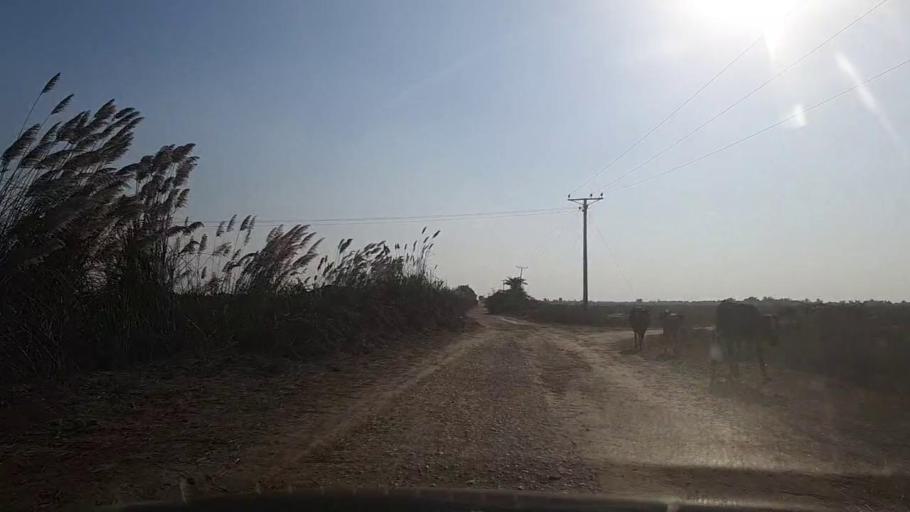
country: PK
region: Sindh
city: Gharo
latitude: 24.7263
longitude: 67.6942
